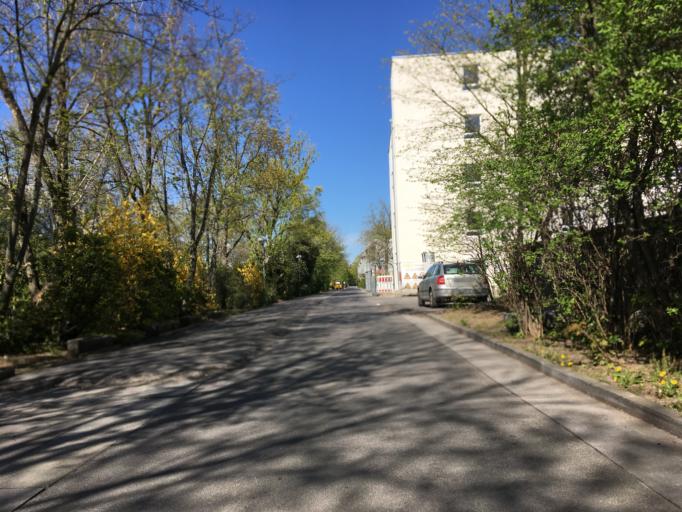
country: DE
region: Berlin
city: Buckow
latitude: 52.4362
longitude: 13.4579
